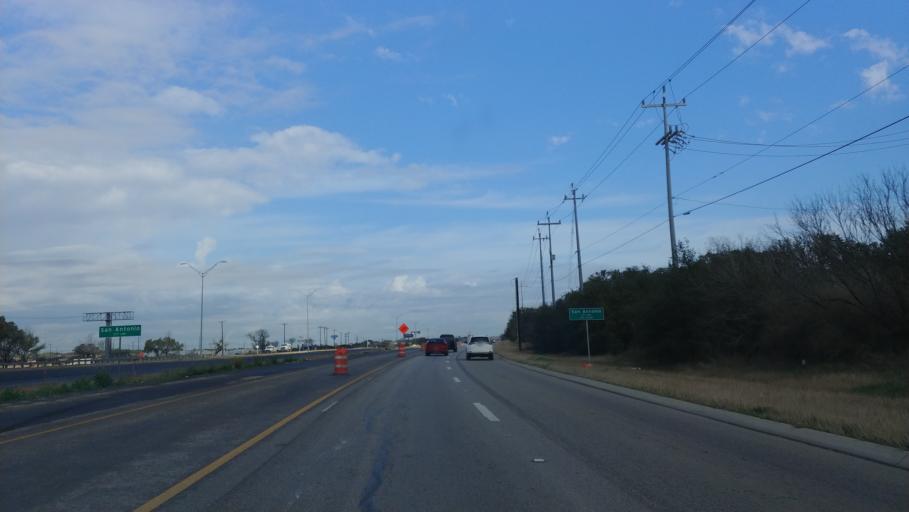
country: US
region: Texas
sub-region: Bexar County
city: Lackland Air Force Base
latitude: 29.4266
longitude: -98.7112
